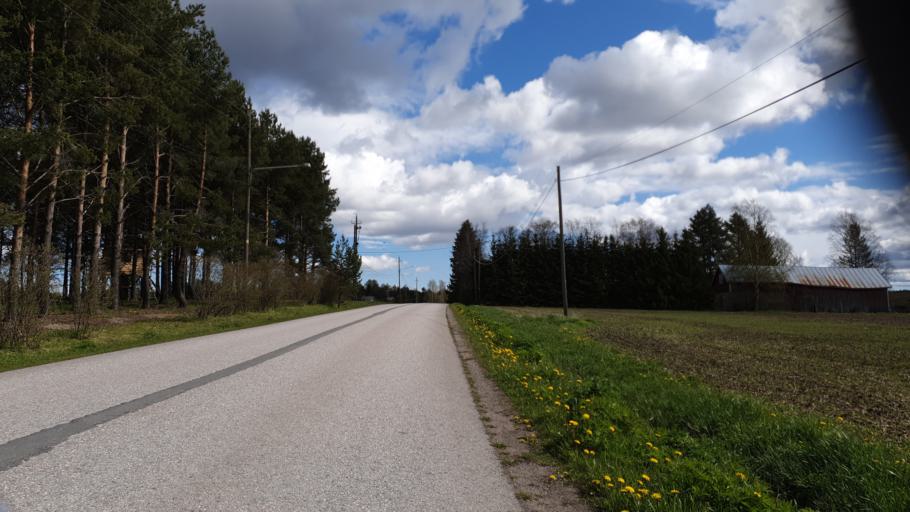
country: FI
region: Uusimaa
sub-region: Helsinki
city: Tuusula
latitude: 60.3959
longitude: 24.9191
